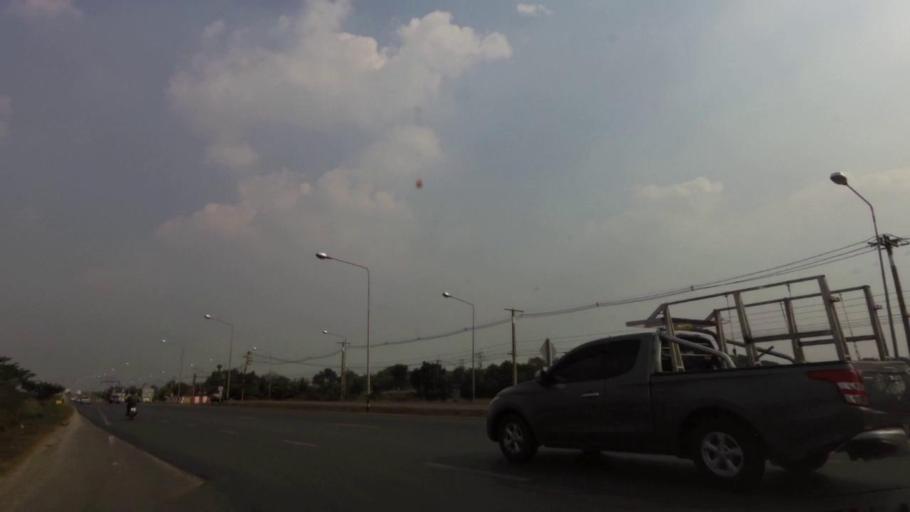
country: TH
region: Phra Nakhon Si Ayutthaya
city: Phra Nakhon Si Ayutthaya
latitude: 14.3049
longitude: 100.5600
